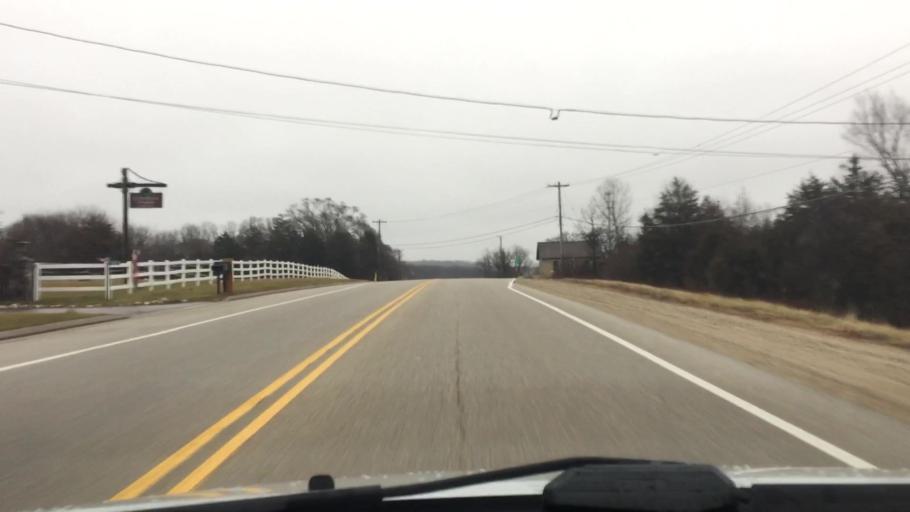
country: US
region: Wisconsin
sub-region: Waukesha County
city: Delafield
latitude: 43.0182
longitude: -88.4246
